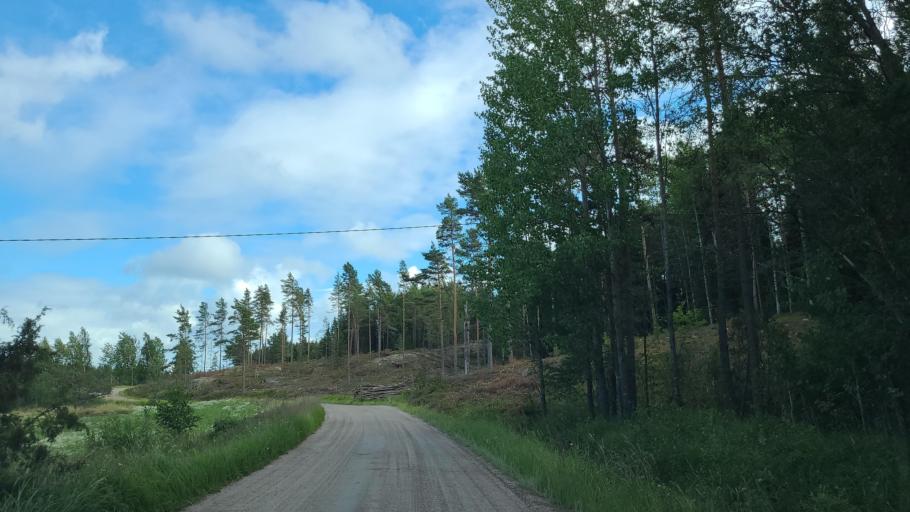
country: FI
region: Varsinais-Suomi
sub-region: Aboland-Turunmaa
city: Nagu
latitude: 60.1515
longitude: 21.7696
